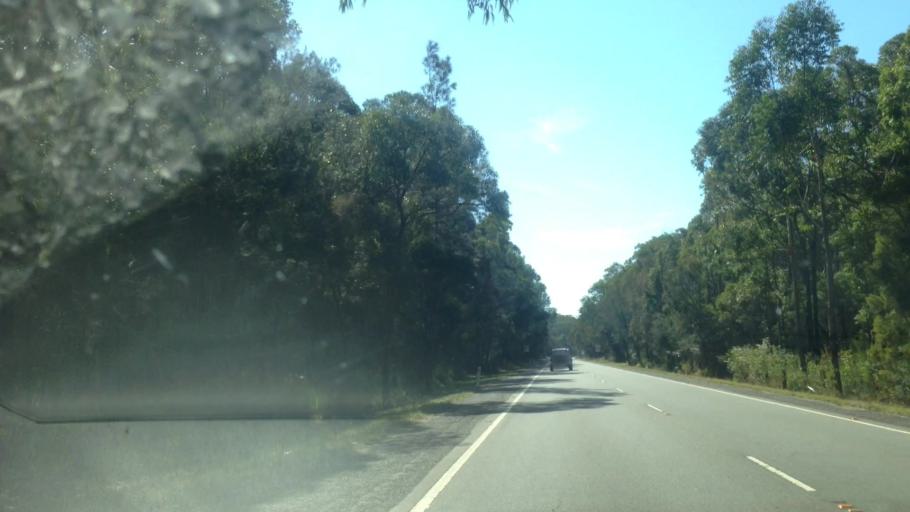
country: AU
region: New South Wales
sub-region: Lake Macquarie Shire
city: Toronto
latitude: -32.9870
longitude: 151.5102
